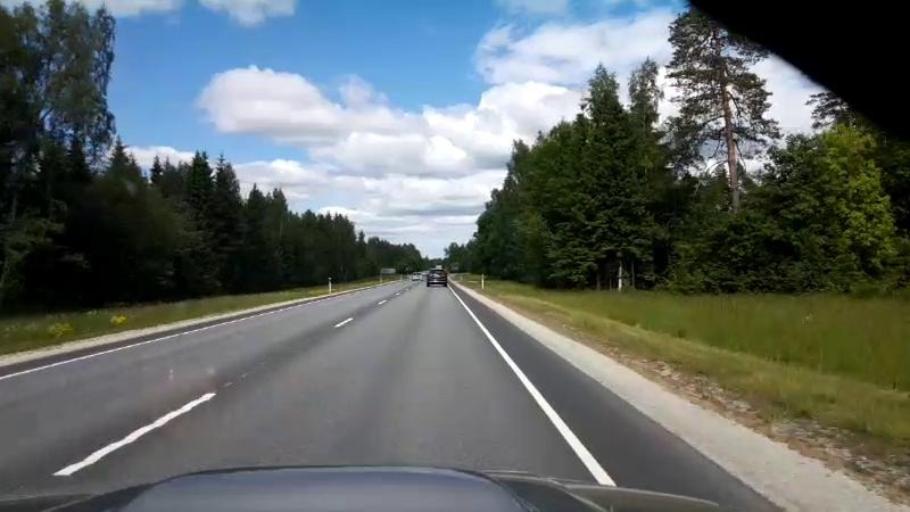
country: EE
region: Harju
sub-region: Nissi vald
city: Riisipere
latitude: 59.0976
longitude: 24.4681
